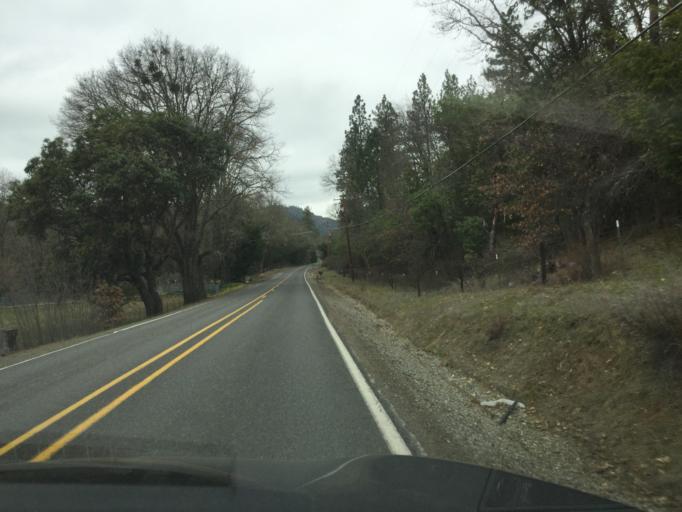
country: US
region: Oregon
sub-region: Jackson County
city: Gold Hill
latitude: 42.4025
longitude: -123.0261
